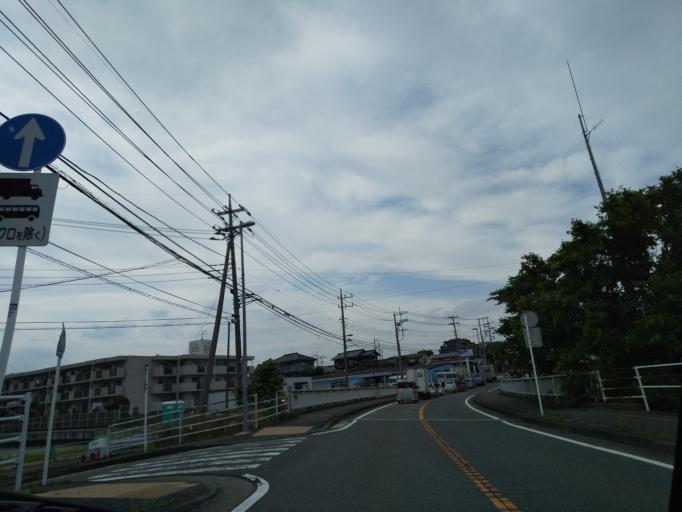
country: JP
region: Kanagawa
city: Atsugi
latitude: 35.4742
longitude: 139.3407
